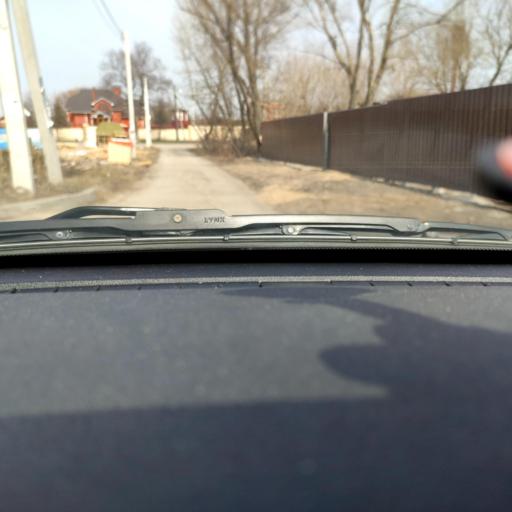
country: RU
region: Voronezj
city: Novaya Usman'
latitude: 51.6260
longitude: 39.4153
